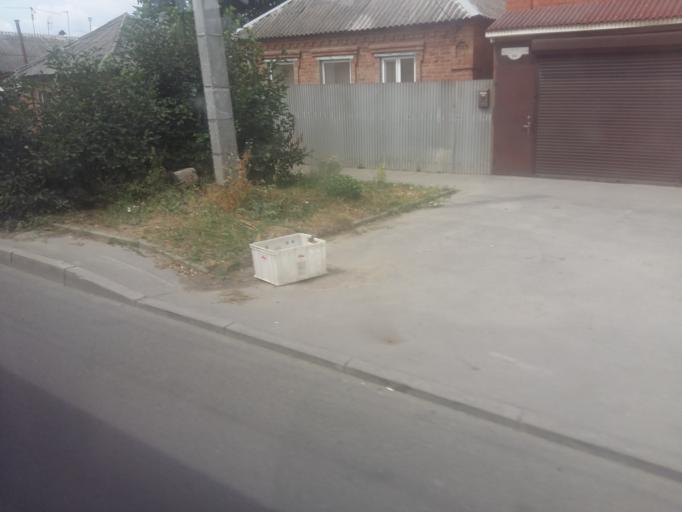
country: RU
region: Rostov
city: Imeni Chkalova
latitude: 47.2814
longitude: 39.7520
